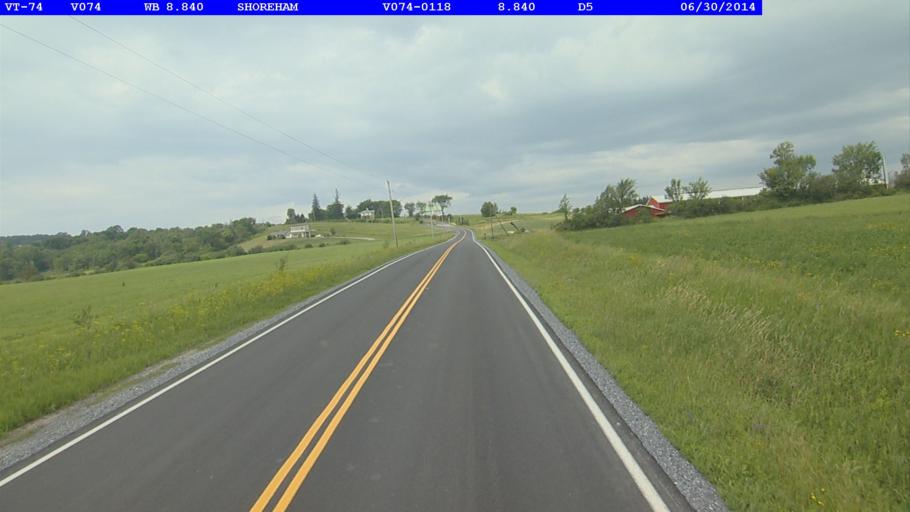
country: US
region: Vermont
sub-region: Addison County
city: Middlebury (village)
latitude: 43.9417
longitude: -73.2777
